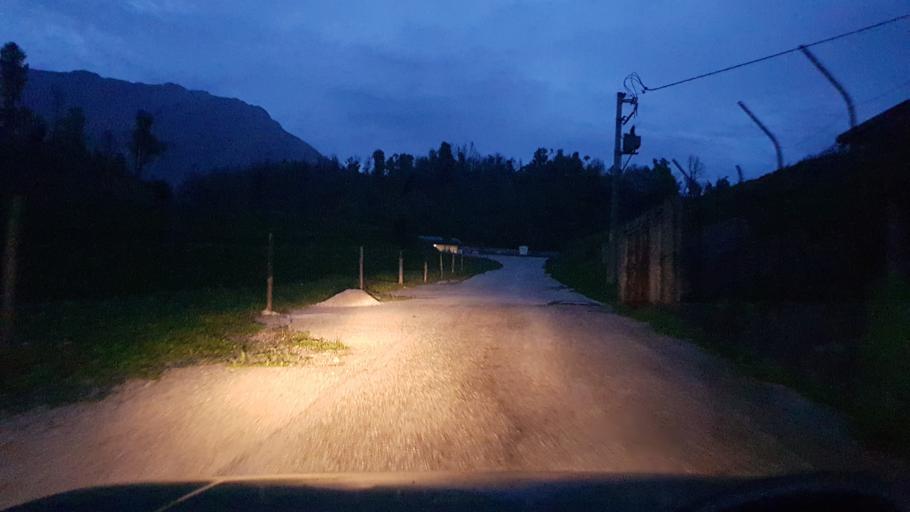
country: IT
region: Friuli Venezia Giulia
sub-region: Provincia di Udine
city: Taipana
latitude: 46.2585
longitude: 13.3506
